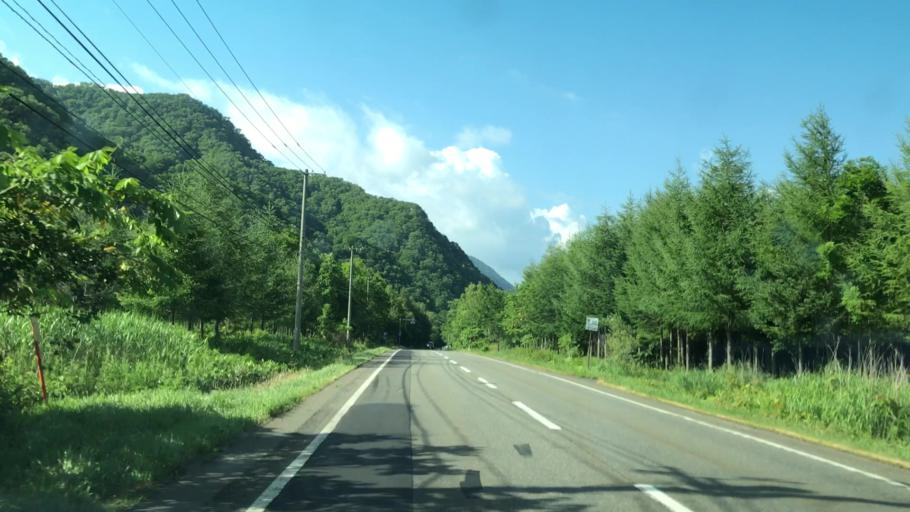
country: JP
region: Hokkaido
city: Shizunai-furukawacho
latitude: 42.8334
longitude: 142.4158
